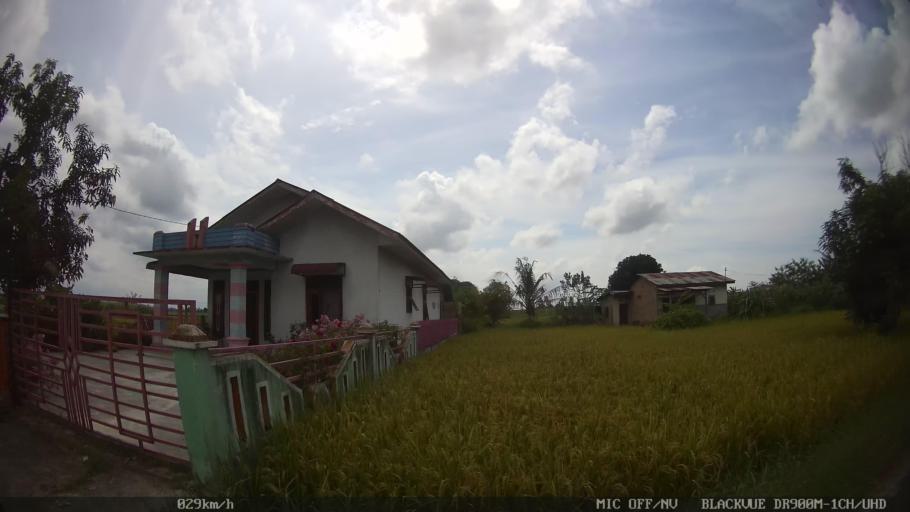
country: ID
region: North Sumatra
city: Percut
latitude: 3.5707
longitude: 98.8502
